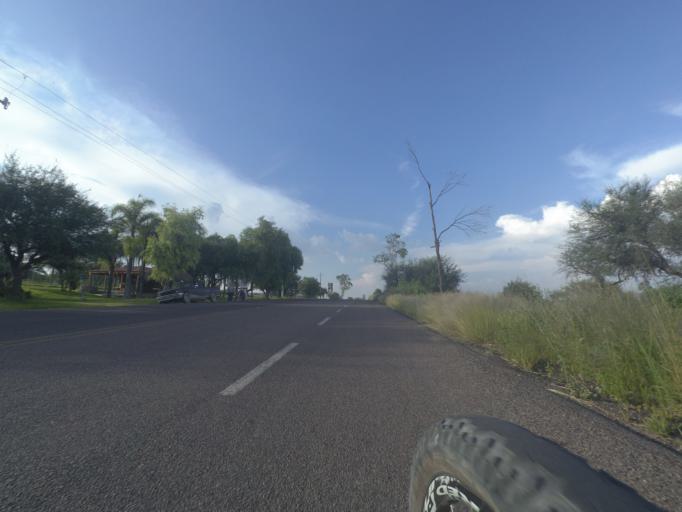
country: MX
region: Aguascalientes
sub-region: Aguascalientes
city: Penuelas (El Cienegal)
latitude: 21.7464
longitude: -102.3511
